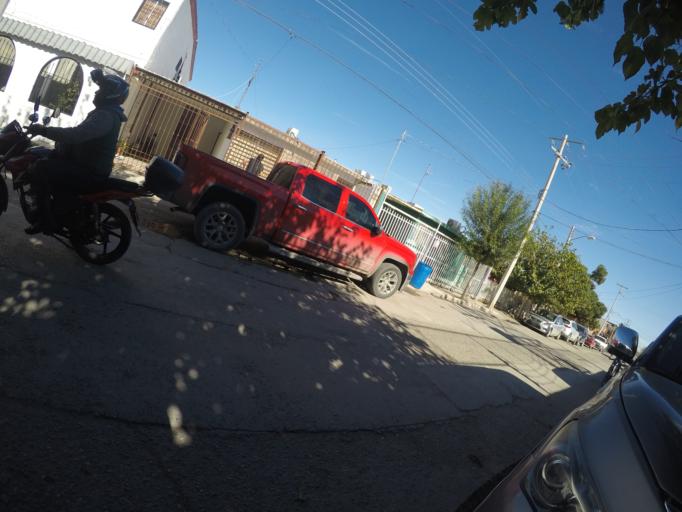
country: MX
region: Chihuahua
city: Ciudad Juarez
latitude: 31.7314
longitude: -106.4273
